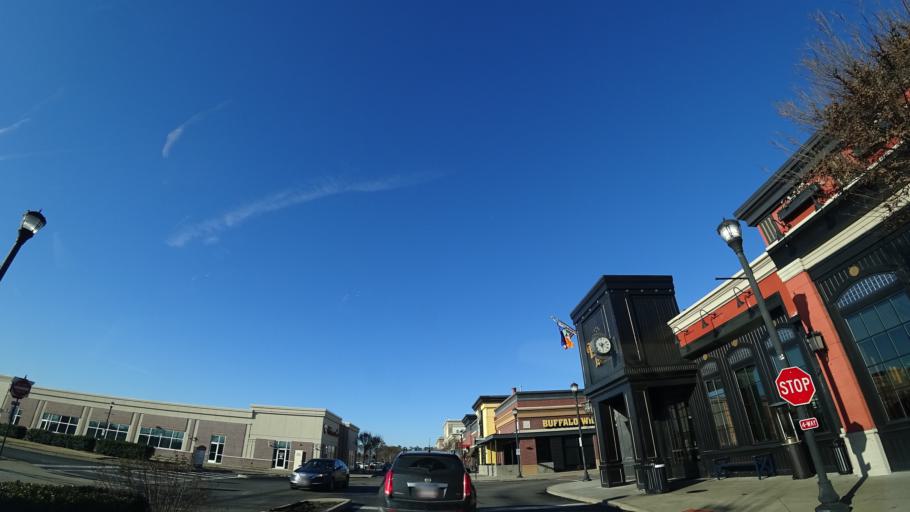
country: US
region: Virginia
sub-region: City of Hampton
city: Hampton
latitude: 37.0439
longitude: -76.3910
